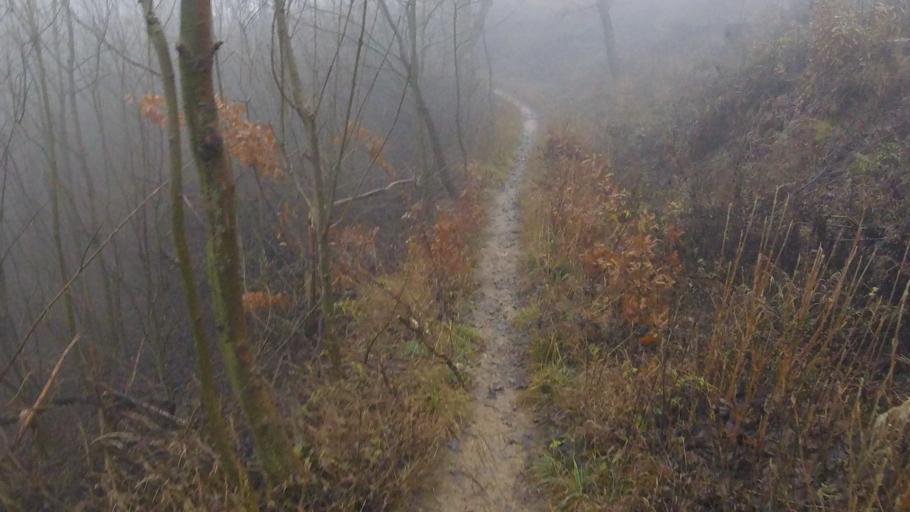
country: HU
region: Pest
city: Biatorbagy
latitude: 47.4562
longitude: 18.8514
